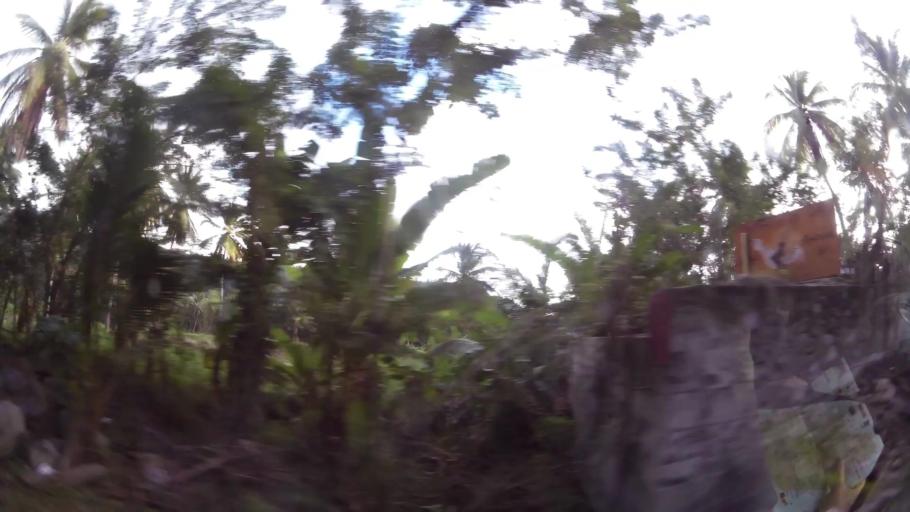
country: DM
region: Saint Joseph
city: Saint Joseph
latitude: 15.3972
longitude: -61.4230
